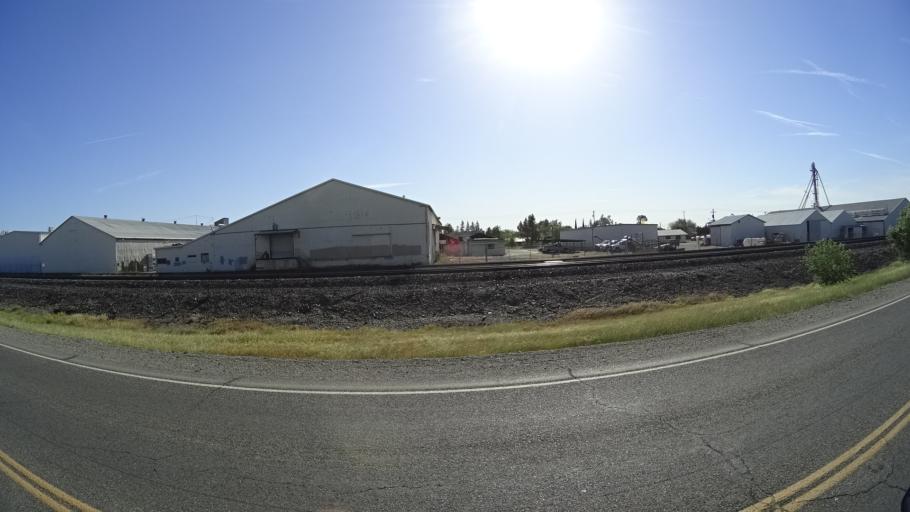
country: US
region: California
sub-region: Glenn County
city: Orland
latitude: 39.7362
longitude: -122.1970
